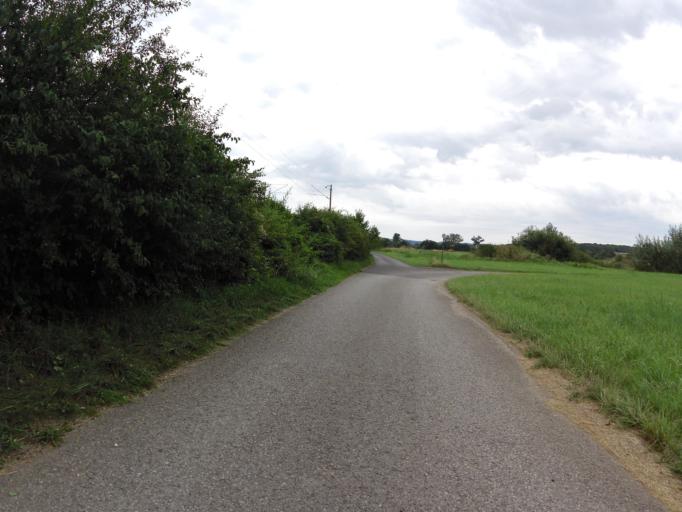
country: DE
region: Bavaria
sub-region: Regierungsbezirk Unterfranken
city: Wonfurt
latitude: 50.0203
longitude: 10.4617
